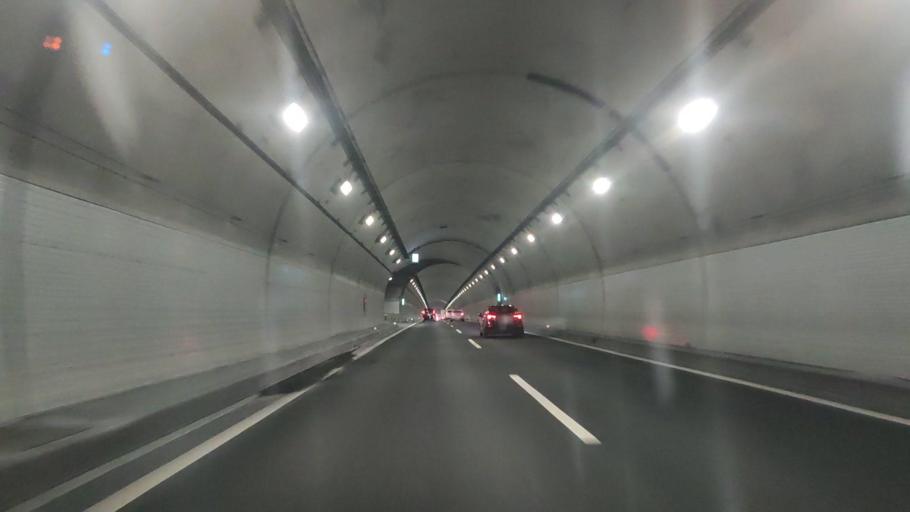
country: JP
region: Fukuoka
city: Kanda
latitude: 33.8089
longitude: 130.9152
